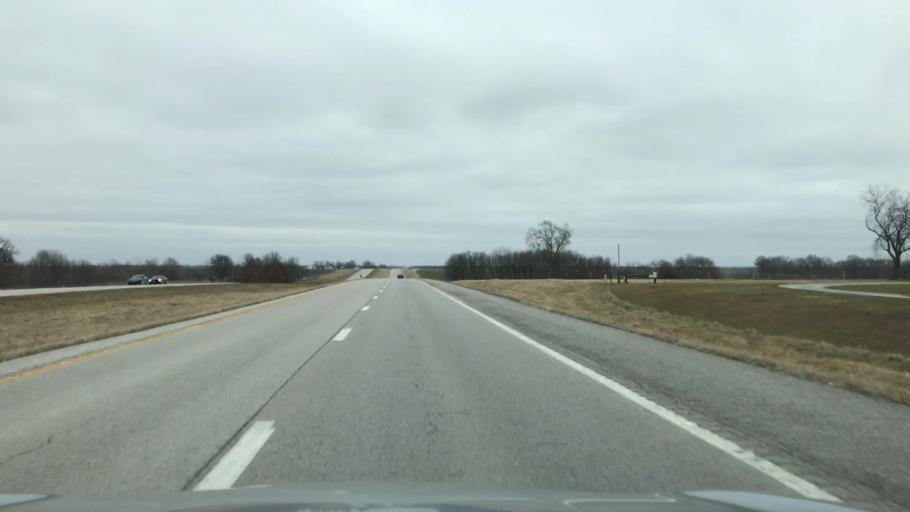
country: US
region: Missouri
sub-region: Livingston County
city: Chillicothe
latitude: 39.7760
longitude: -93.4881
